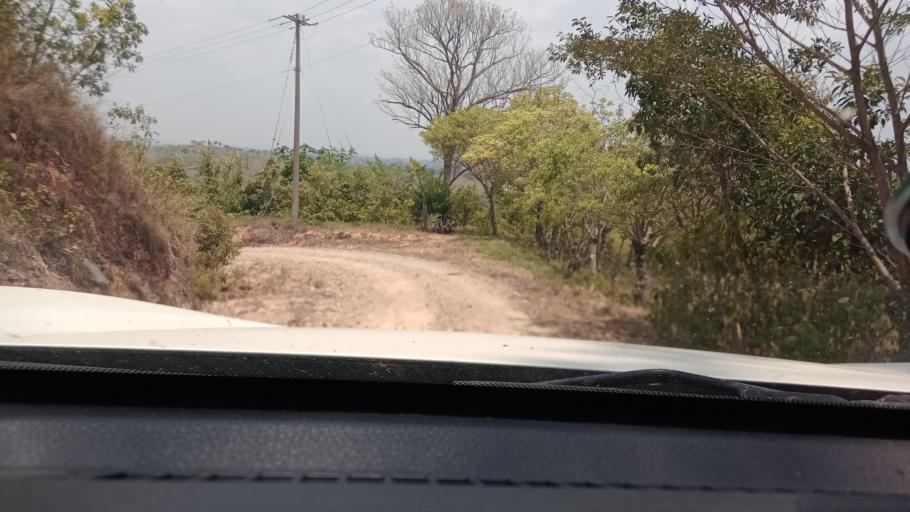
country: MX
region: Tabasco
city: Chontalpa
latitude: 17.5558
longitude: -93.7317
